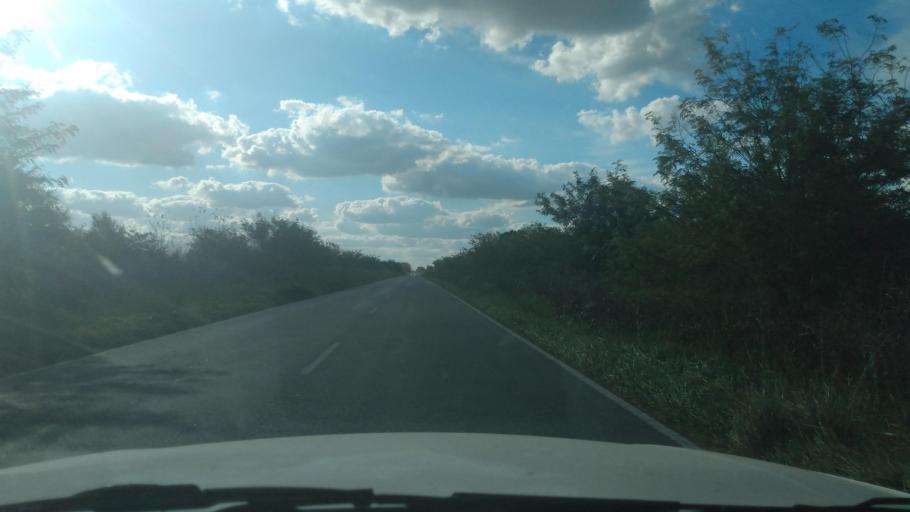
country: AR
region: Buenos Aires
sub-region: Partido de Mercedes
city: Mercedes
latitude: -34.7626
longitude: -59.3750
